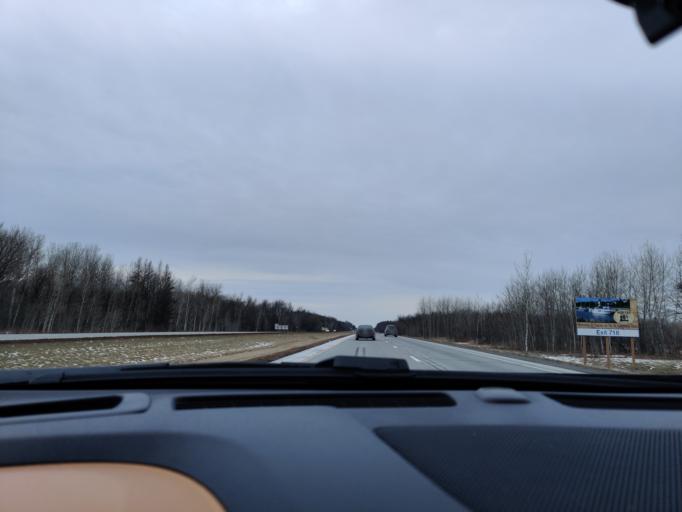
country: US
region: New York
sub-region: St. Lawrence County
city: Ogdensburg
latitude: 44.7974
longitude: -75.4269
